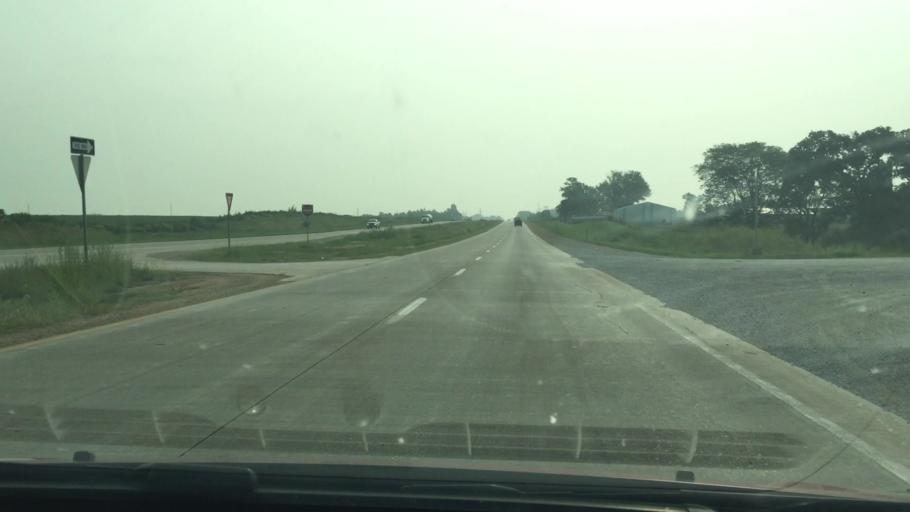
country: US
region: Iowa
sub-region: Scott County
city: Blue Grass
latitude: 41.5088
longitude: -90.7176
